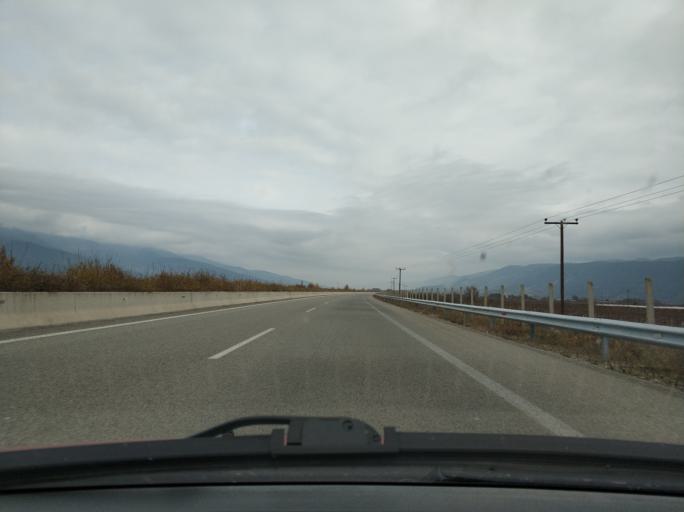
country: GR
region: Central Macedonia
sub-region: Nomos Serron
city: Rodolivos
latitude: 40.8192
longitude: 24.0562
